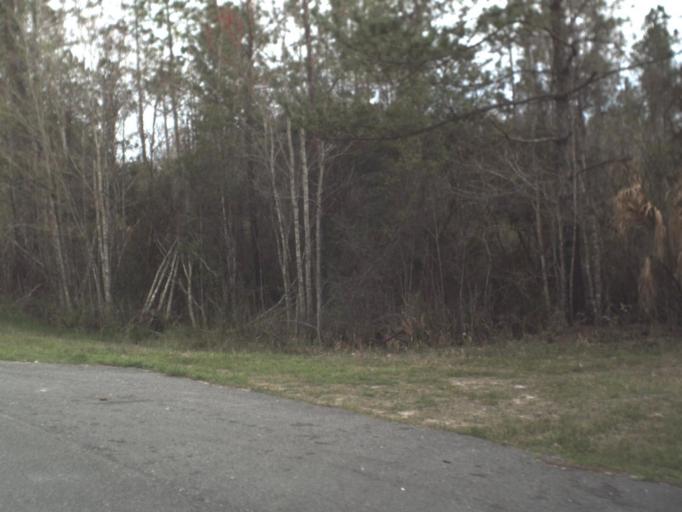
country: US
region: Florida
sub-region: Leon County
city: Woodville
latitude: 30.1874
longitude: -84.0243
